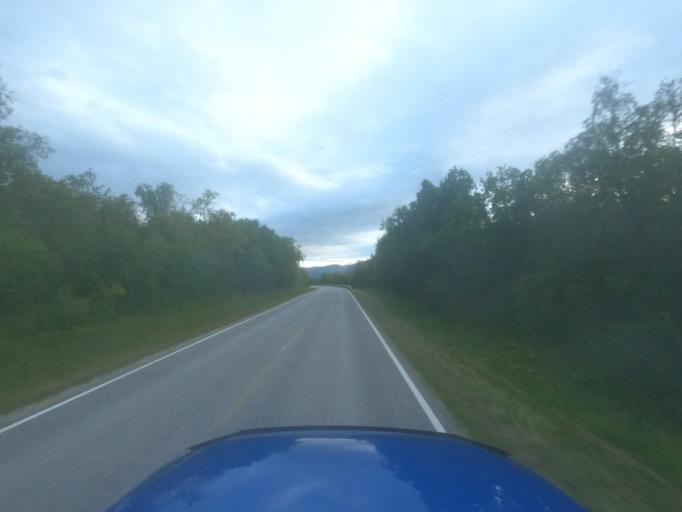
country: NO
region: Finnmark Fylke
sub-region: Porsanger
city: Lakselv
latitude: 70.0235
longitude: 24.9682
